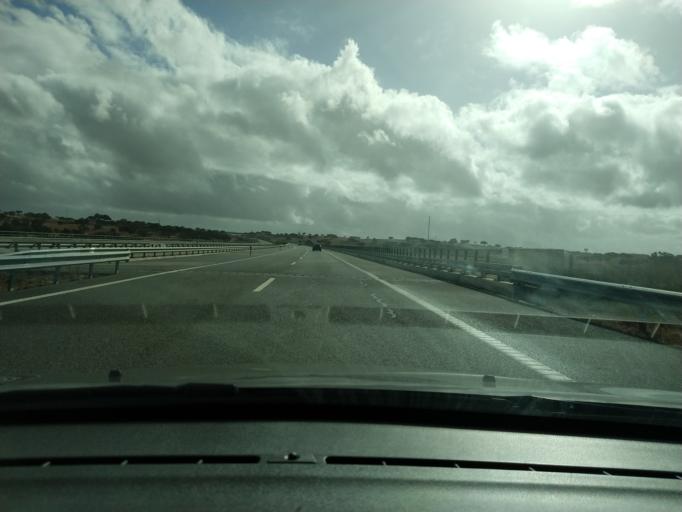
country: PT
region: Beja
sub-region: Ourique
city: Ourique
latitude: 37.5759
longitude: -8.1883
